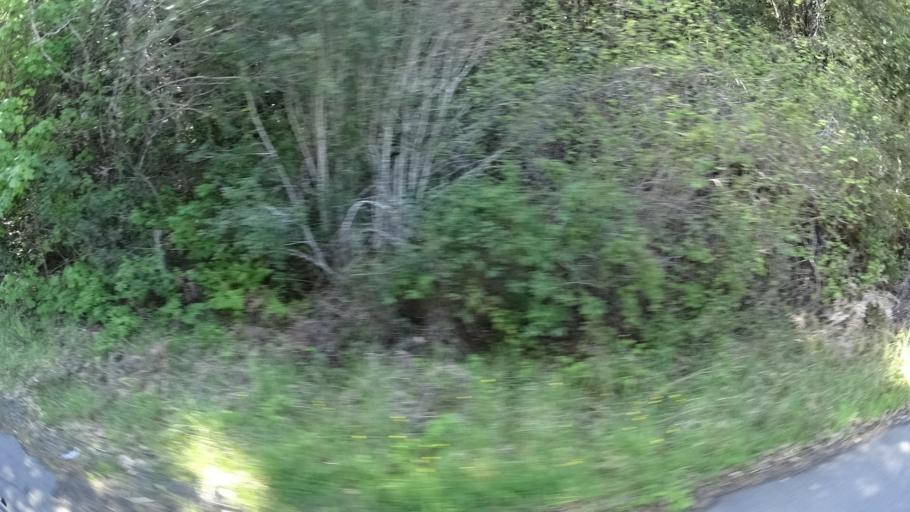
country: US
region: California
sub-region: Humboldt County
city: Rio Dell
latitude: 40.2313
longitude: -124.1144
